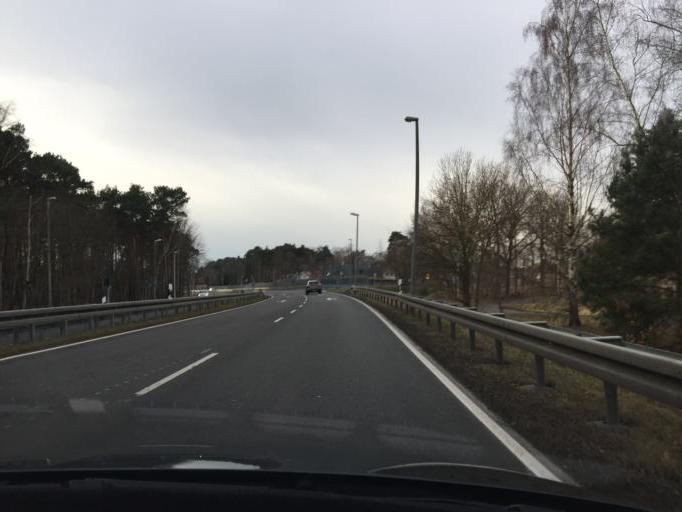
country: DE
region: Brandenburg
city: Peitz
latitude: 51.8079
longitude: 14.3866
